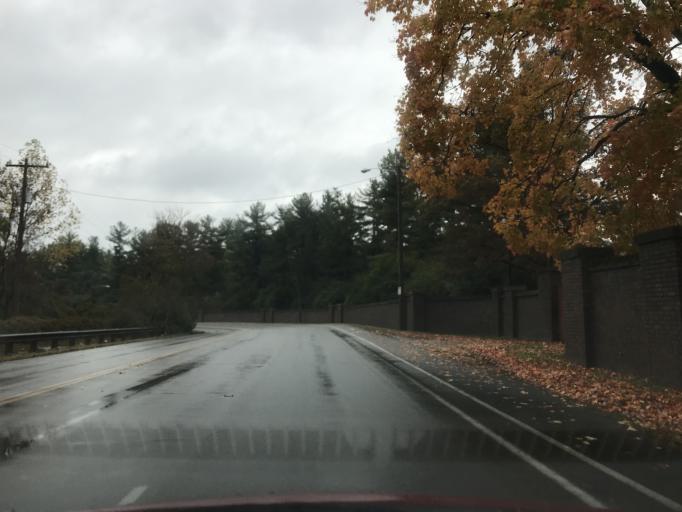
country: US
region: Indiana
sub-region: Clark County
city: Jeffersonville
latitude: 38.2469
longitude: -85.7074
